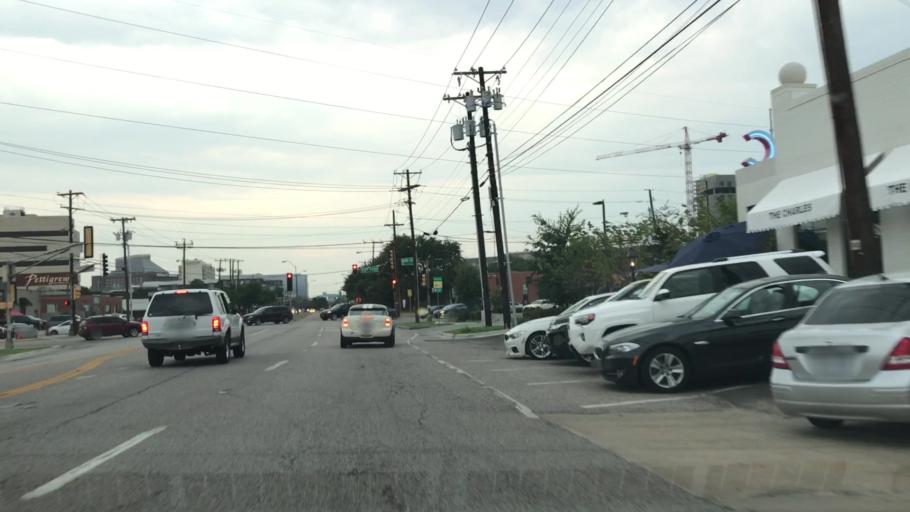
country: US
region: Texas
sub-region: Dallas County
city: Dallas
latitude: 32.7928
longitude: -96.8220
